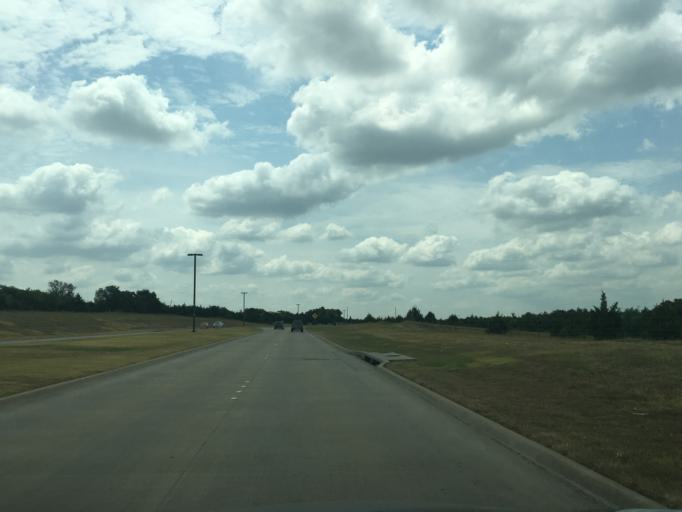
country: US
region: Texas
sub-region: Rockwall County
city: Rockwall
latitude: 32.9339
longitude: -96.4393
